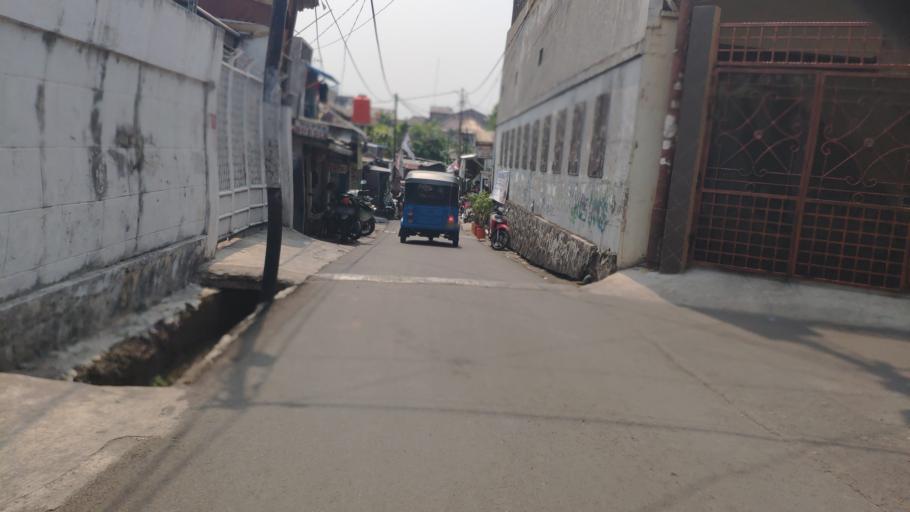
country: ID
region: Jakarta Raya
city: Jakarta
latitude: -6.2564
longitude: 106.7953
